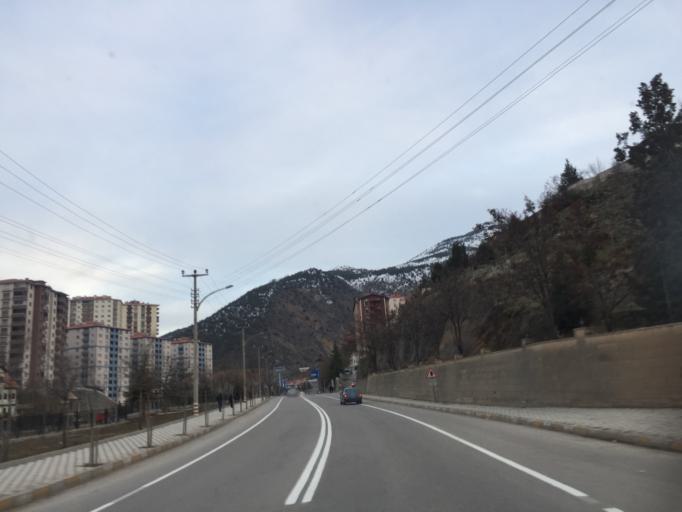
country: TR
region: Gumushane
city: Gumushkhane
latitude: 40.4655
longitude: 39.4636
